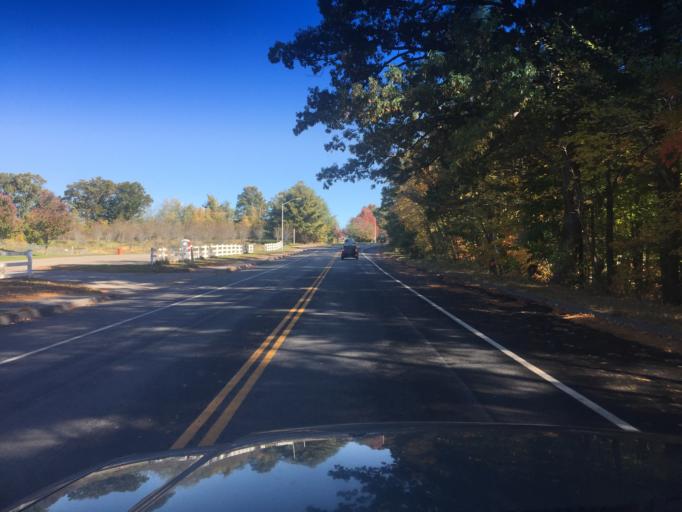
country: US
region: Massachusetts
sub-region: Middlesex County
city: Hudson
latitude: 42.3800
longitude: -71.5600
